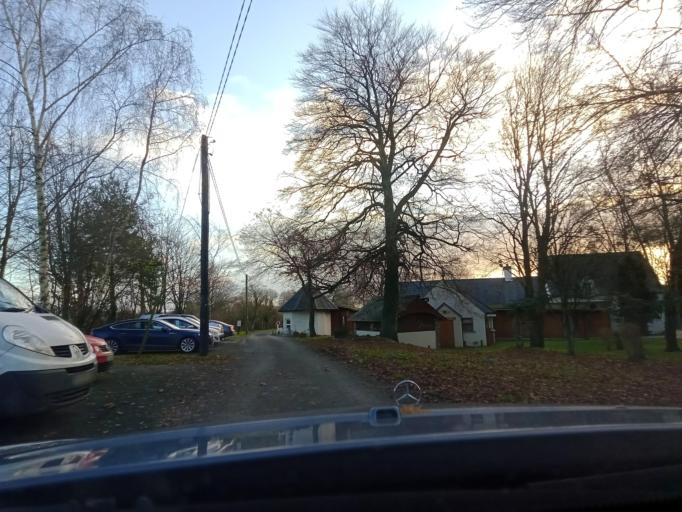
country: IE
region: Leinster
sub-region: Kilkenny
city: Callan
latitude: 52.5063
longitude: -7.3382
